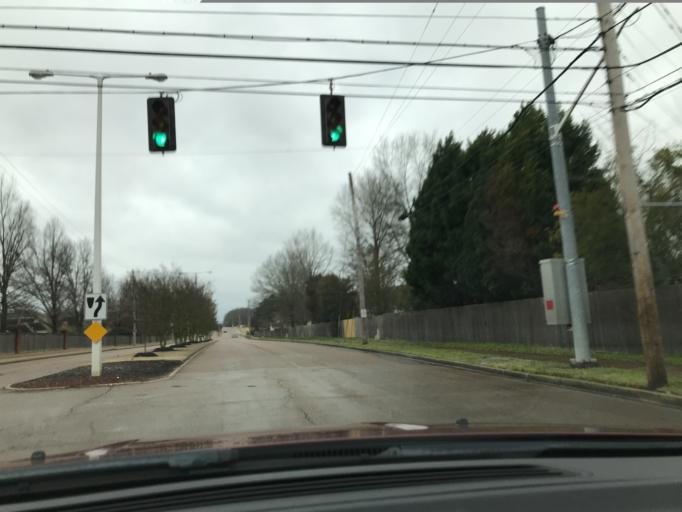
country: US
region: Tennessee
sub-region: Shelby County
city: Collierville
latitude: 35.0747
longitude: -89.6855
